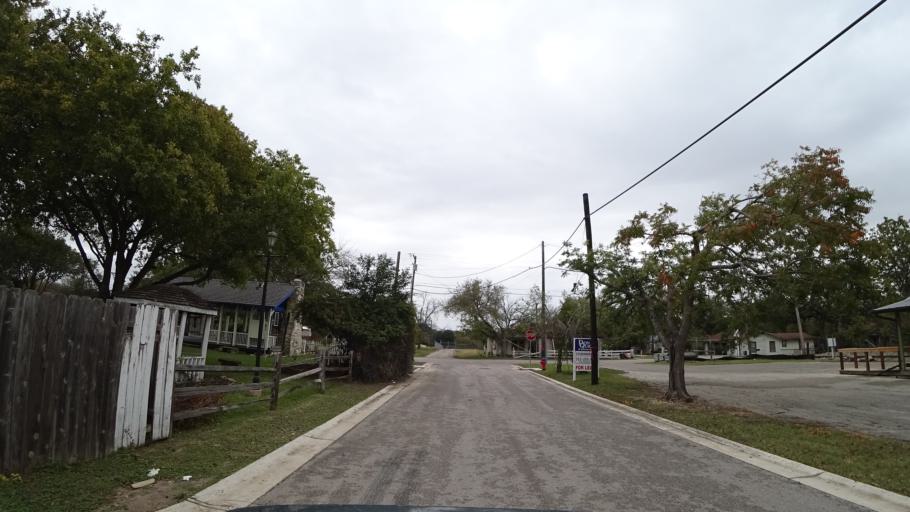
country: US
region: Texas
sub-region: Williamson County
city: Round Rock
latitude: 30.5150
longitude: -97.6906
